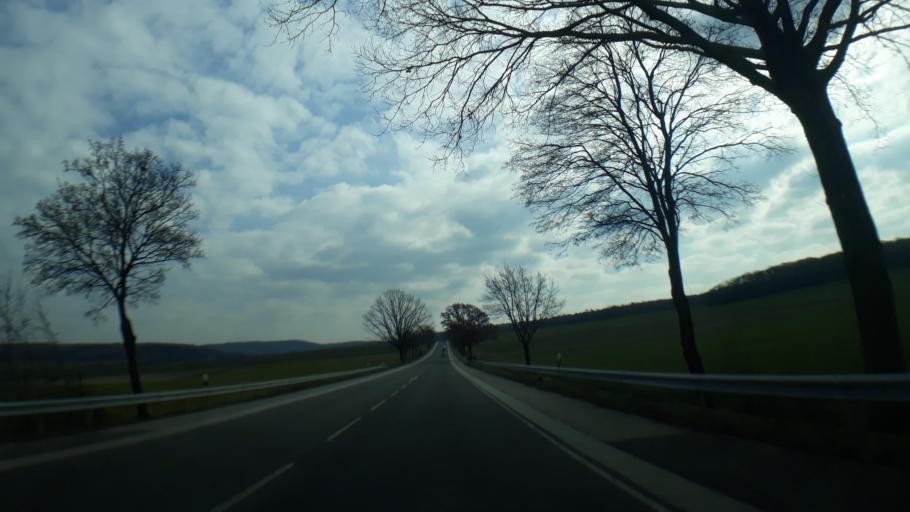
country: DE
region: North Rhine-Westphalia
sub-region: Regierungsbezirk Koln
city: Rheinbach
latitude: 50.6059
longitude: 6.8607
